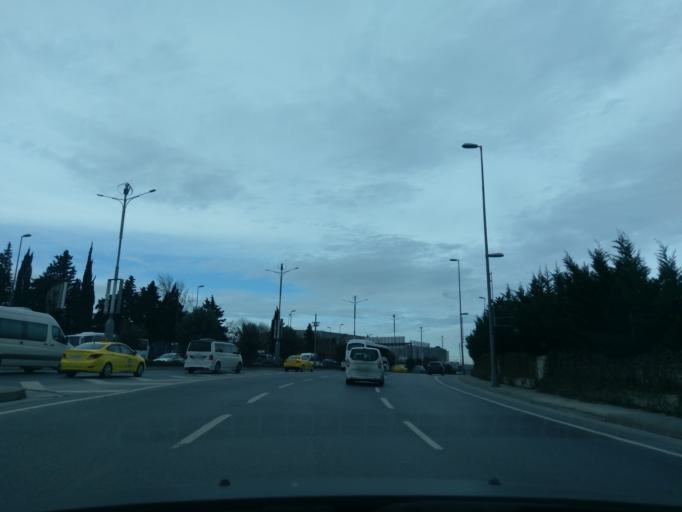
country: TR
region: Istanbul
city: Bahcelievler
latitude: 40.9844
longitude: 28.8202
